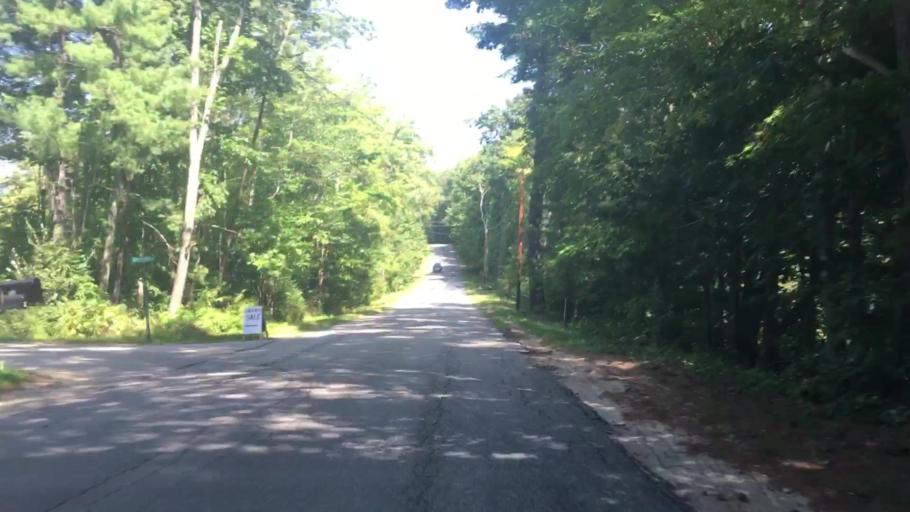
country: US
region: Maine
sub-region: Kennebec County
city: Monmouth
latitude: 44.2062
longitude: -69.9530
